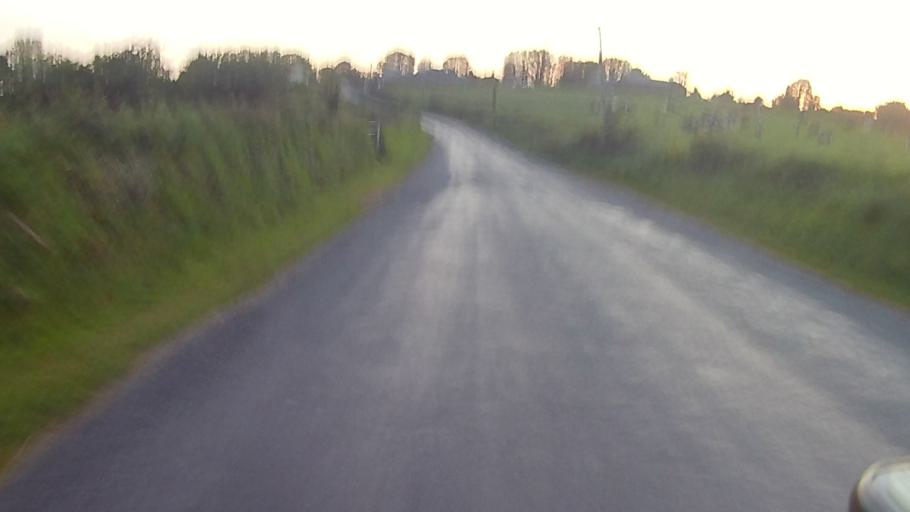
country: IE
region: Munster
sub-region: County Cork
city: Carrigtwohill
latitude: 51.9719
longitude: -8.2501
